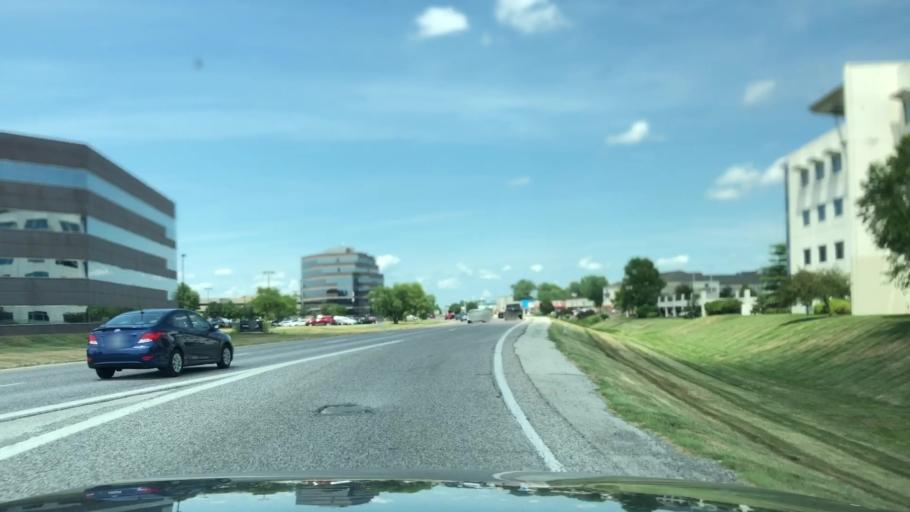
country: US
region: Missouri
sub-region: Saint Charles County
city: Saint Charles
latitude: 38.7587
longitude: -90.4567
